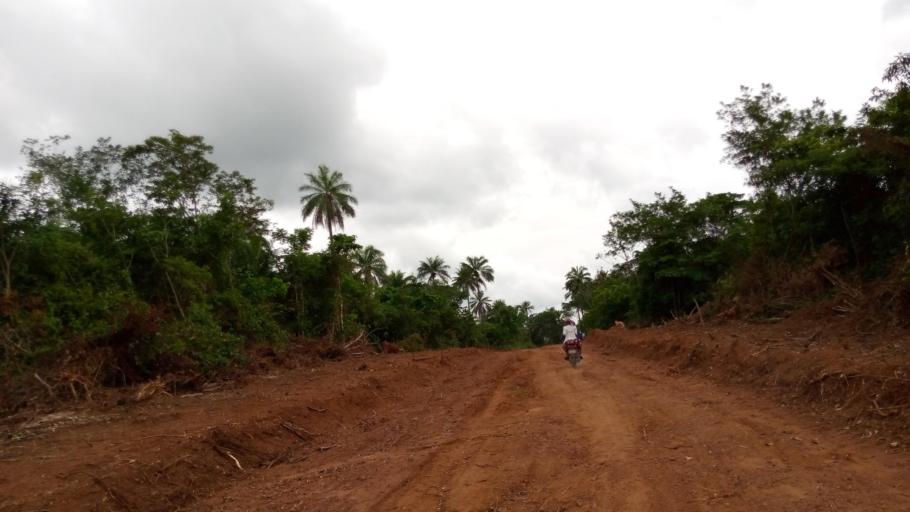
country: SL
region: Southern Province
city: Moyamba
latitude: 8.1951
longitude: -12.5398
